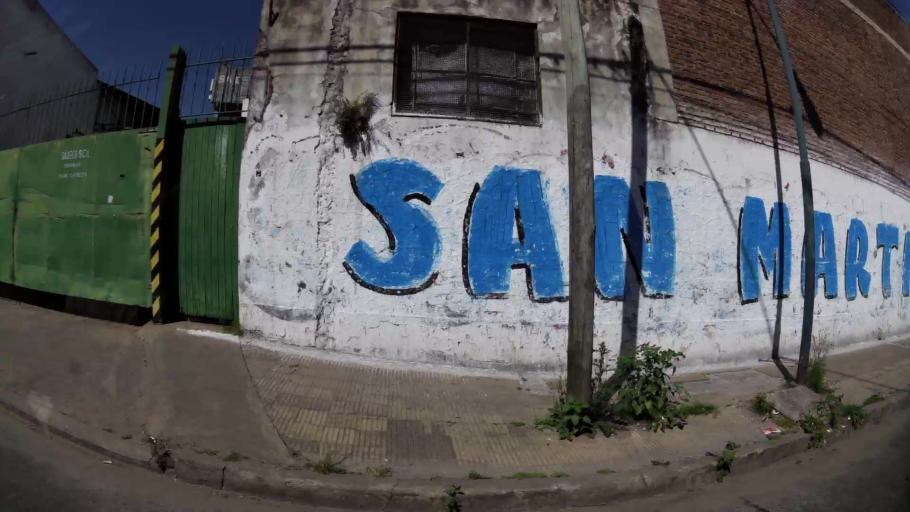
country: AR
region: Buenos Aires
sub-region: Partido de General San Martin
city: General San Martin
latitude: -34.5481
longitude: -58.5304
